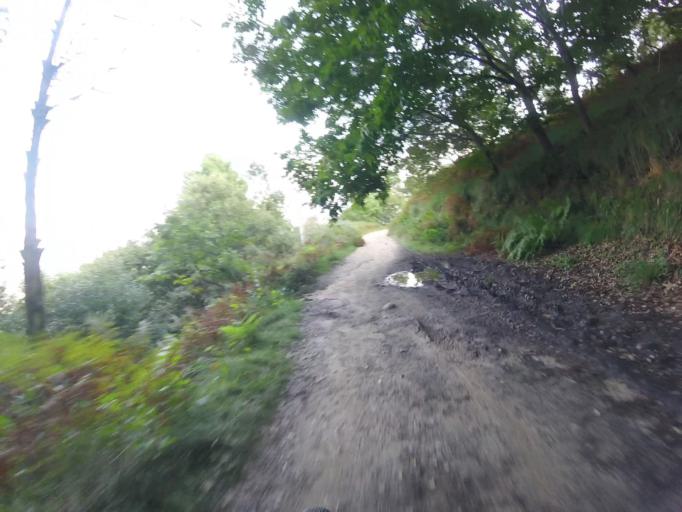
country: ES
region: Basque Country
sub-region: Provincia de Guipuzcoa
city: Fuenterrabia
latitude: 43.3638
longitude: -1.8246
